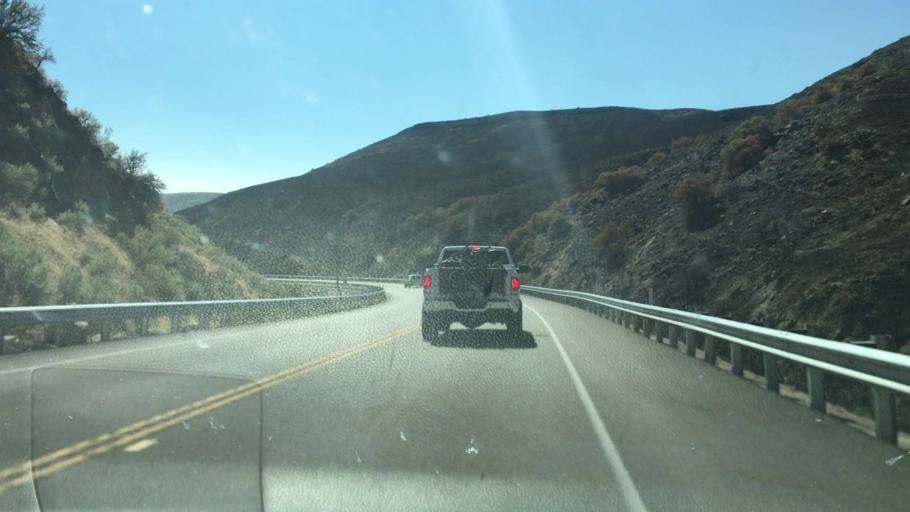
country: US
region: Idaho
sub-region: Ada County
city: Eagle
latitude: 43.7606
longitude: -116.2702
